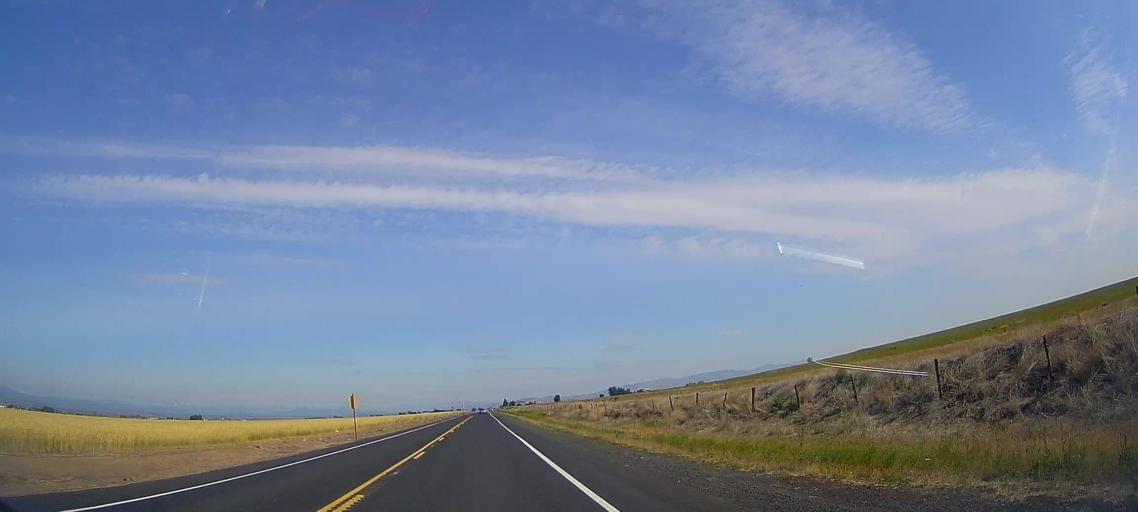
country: US
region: Oregon
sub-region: Jefferson County
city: Madras
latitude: 44.6690
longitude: -121.1390
